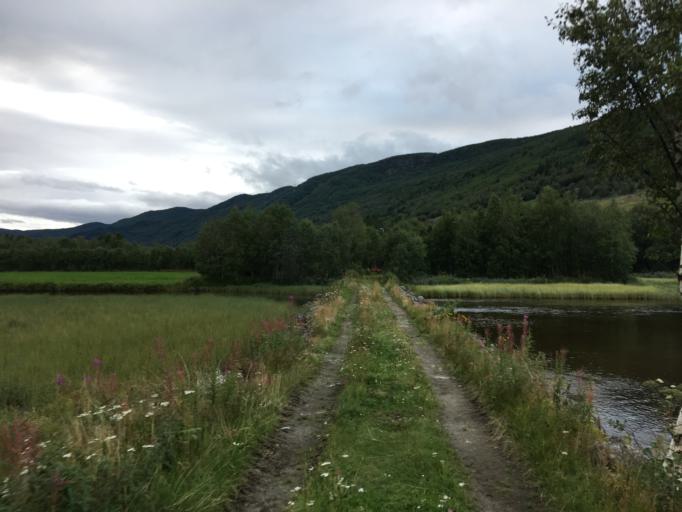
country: NO
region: Buskerud
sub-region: Hol
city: Hol
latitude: 60.6176
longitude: 8.2246
